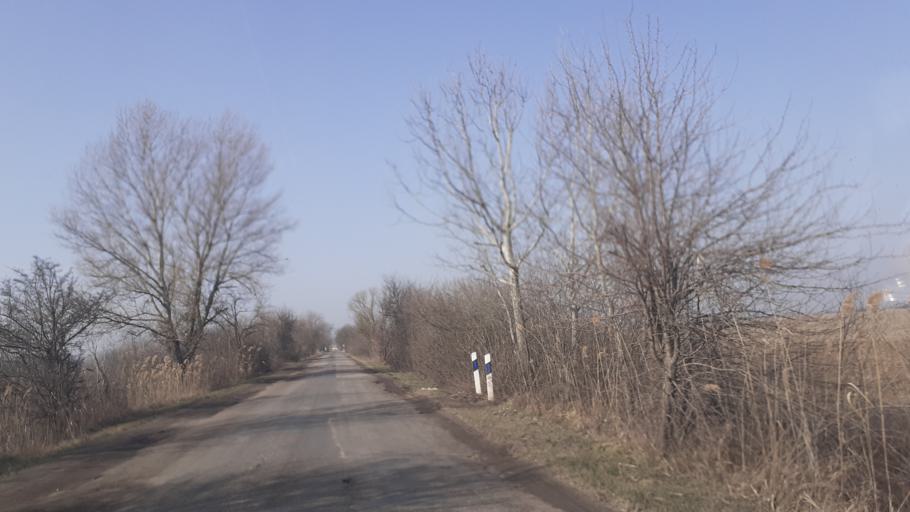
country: HU
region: Pest
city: Dabas
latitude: 47.0597
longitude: 19.2926
